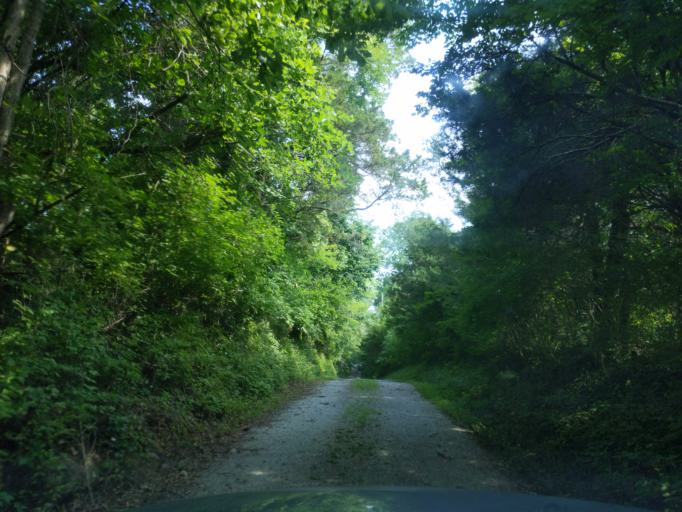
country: US
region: Tennessee
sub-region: Williamson County
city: Brentwood Estates
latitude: 36.0144
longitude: -86.7549
